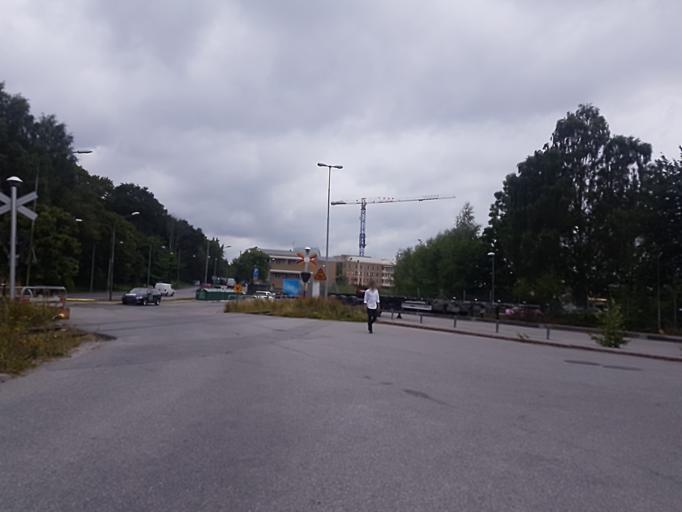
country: SE
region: Stockholm
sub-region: Lidingo
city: Lidingoe
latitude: 59.3397
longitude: 18.1186
